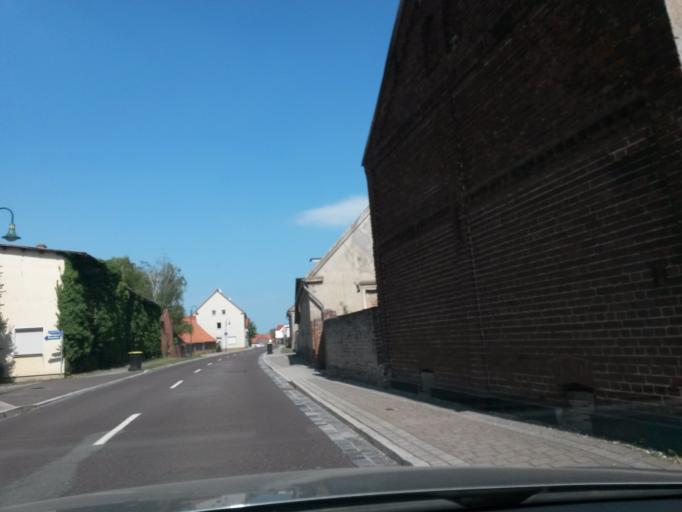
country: DE
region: Saxony-Anhalt
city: Jerichow
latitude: 52.4377
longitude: 11.9990
